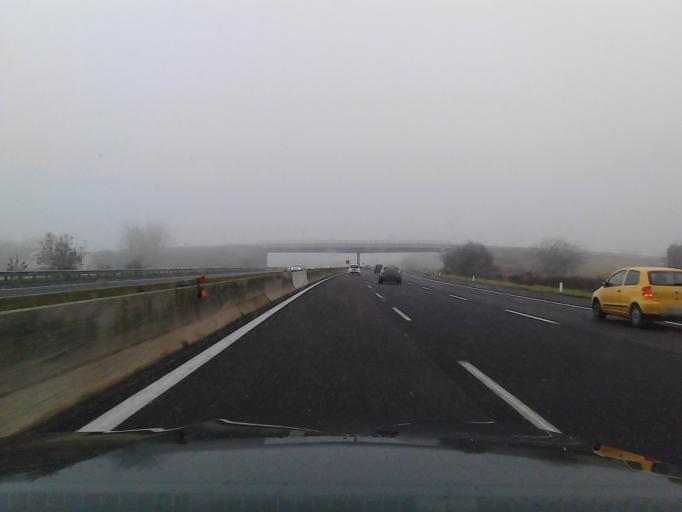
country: IT
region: Emilia-Romagna
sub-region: Provincia di Bologna
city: Imola
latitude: 44.3970
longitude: 11.7002
